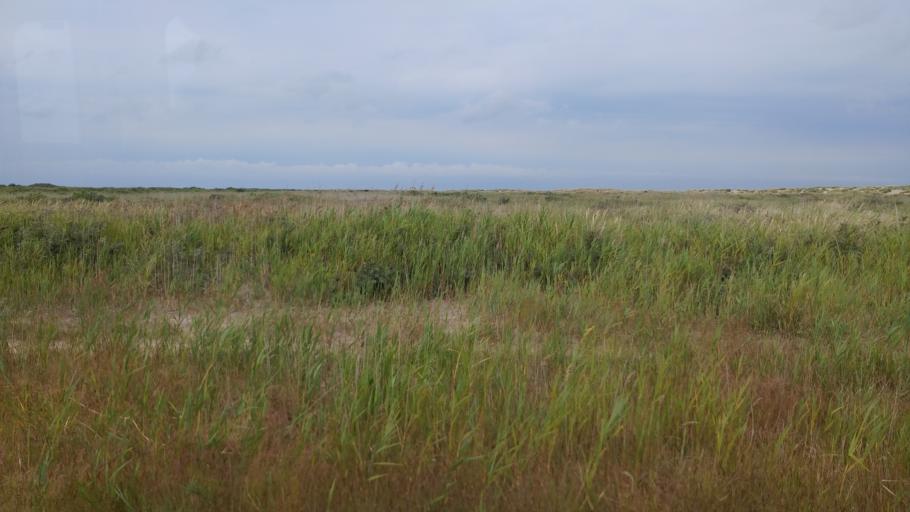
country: DK
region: North Denmark
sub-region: Frederikshavn Kommune
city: Skagen
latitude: 57.7466
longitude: 10.6380
